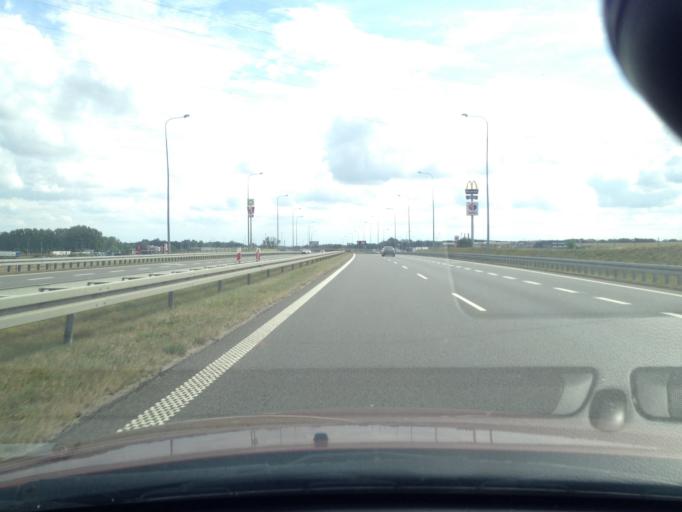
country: PL
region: West Pomeranian Voivodeship
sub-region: Powiat gryfinski
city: Gryfino
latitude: 53.3096
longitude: 14.5805
